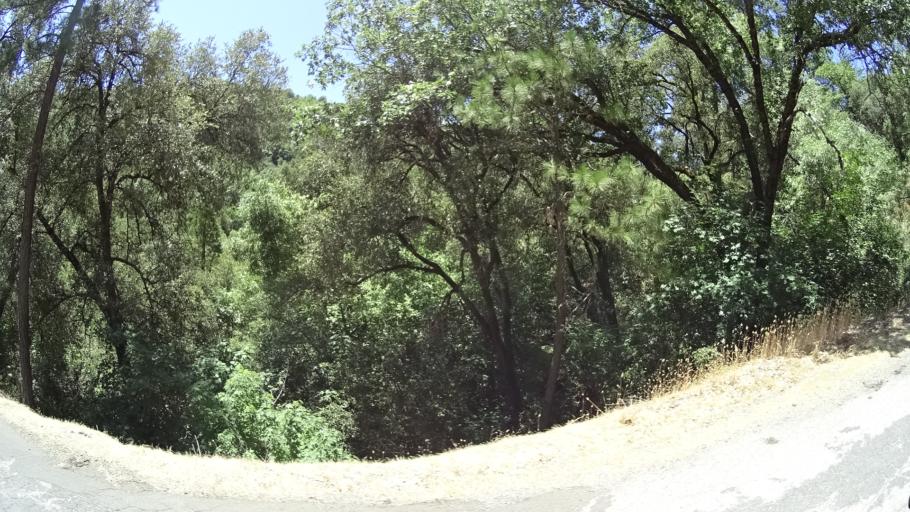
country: US
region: California
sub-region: Calaveras County
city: Forest Meadows
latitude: 38.2046
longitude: -120.4525
